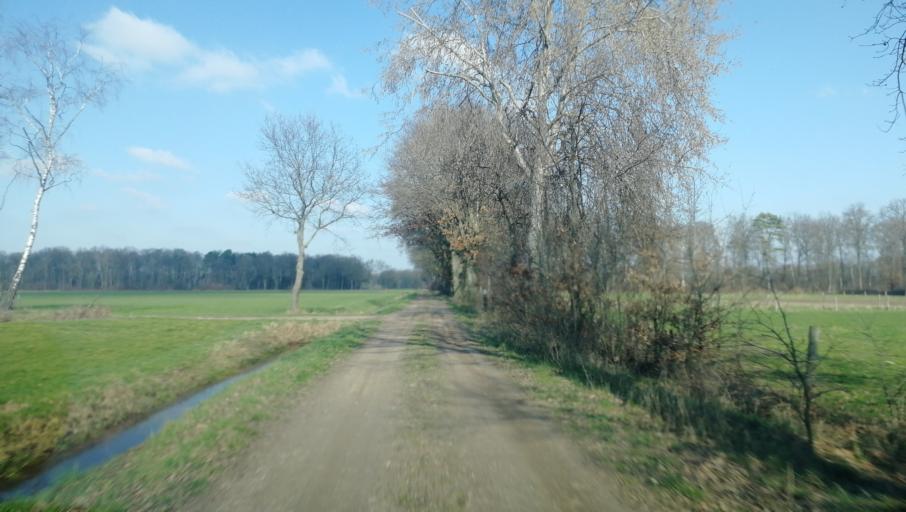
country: NL
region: Limburg
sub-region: Gemeente Venlo
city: Venlo
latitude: 51.4146
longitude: 6.2064
